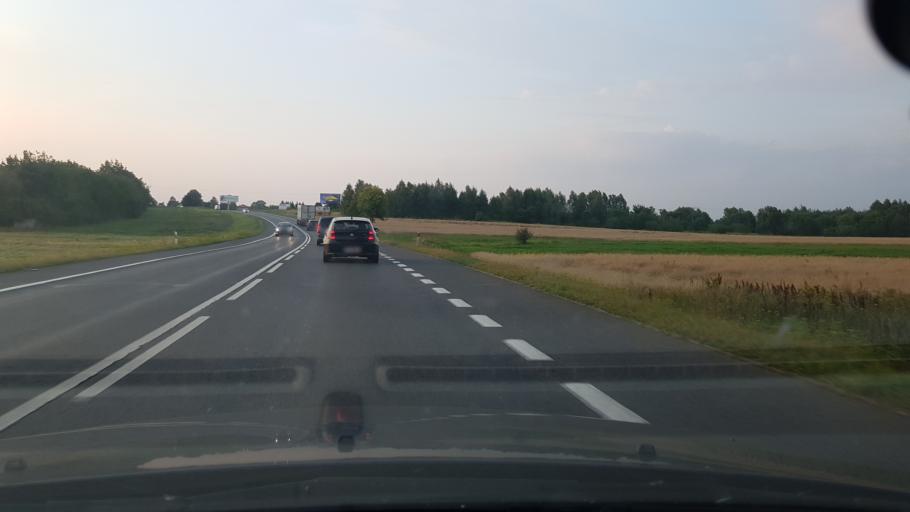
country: PL
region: Masovian Voivodeship
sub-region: Powiat mlawski
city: Mlawa
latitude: 53.1071
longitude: 20.4004
